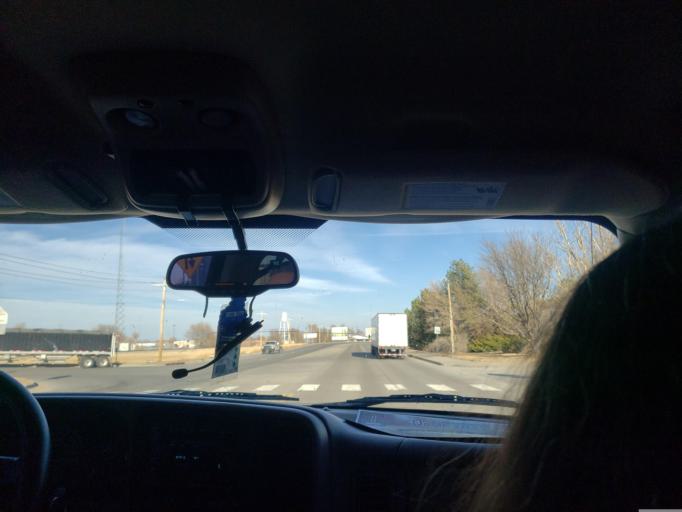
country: US
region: Oklahoma
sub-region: Texas County
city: Goodwell
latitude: 36.5001
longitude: -101.7874
